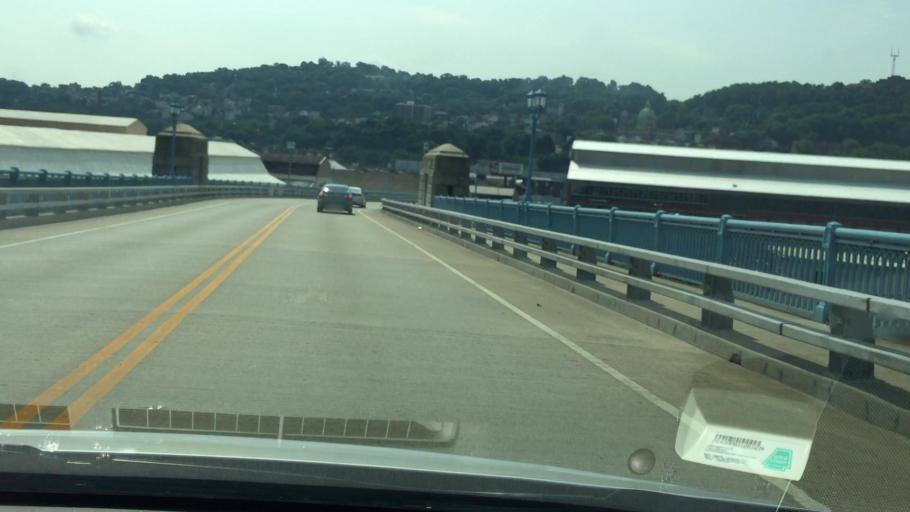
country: US
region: Pennsylvania
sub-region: Allegheny County
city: Millvale
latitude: 40.4626
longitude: -79.9751
